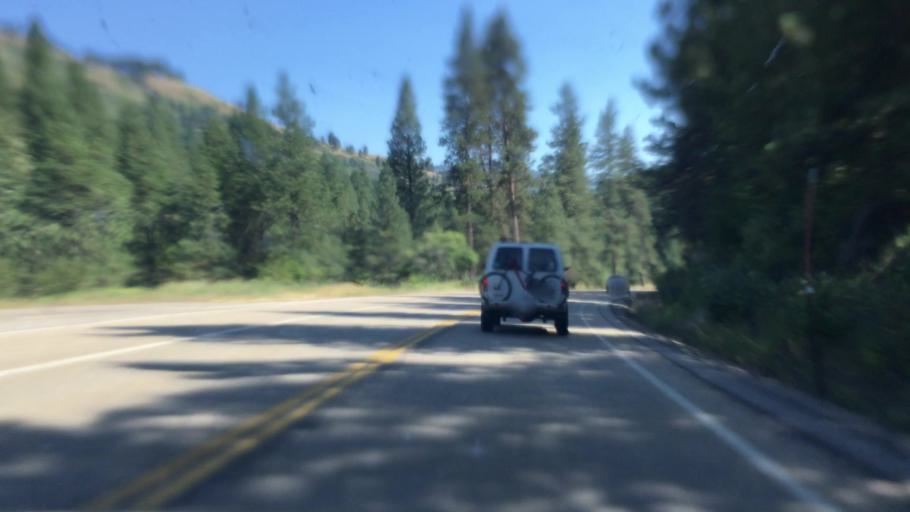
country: US
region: Idaho
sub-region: Valley County
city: Cascade
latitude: 44.1351
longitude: -116.1157
